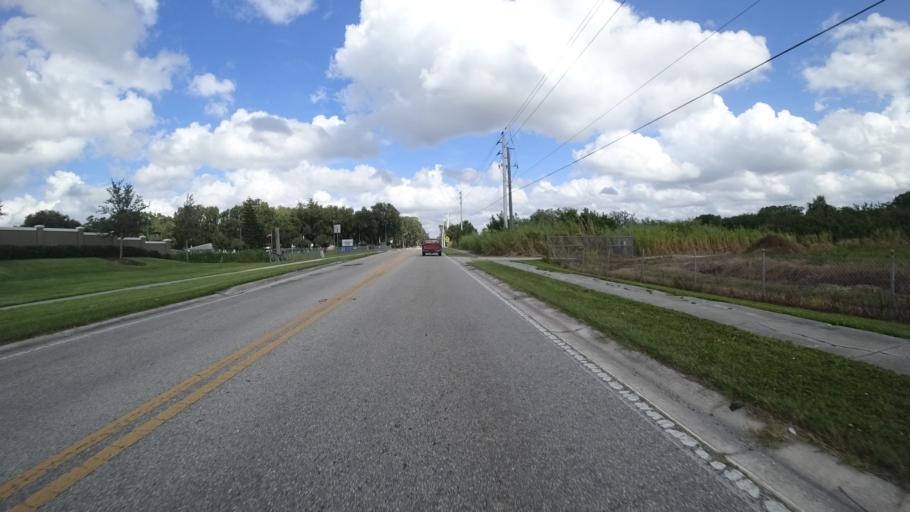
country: US
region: Florida
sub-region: Manatee County
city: Samoset
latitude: 27.4800
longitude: -82.5302
